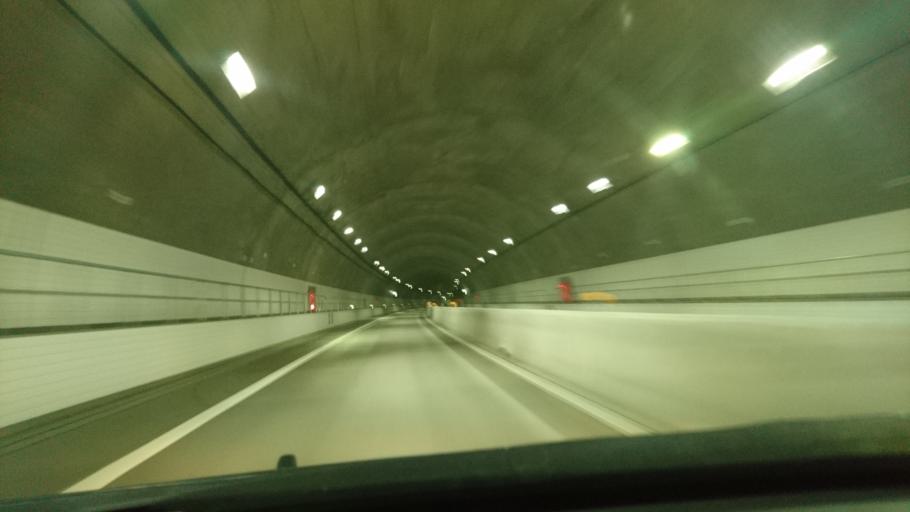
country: JP
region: Iwate
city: Miyako
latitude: 39.8066
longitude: 141.9556
